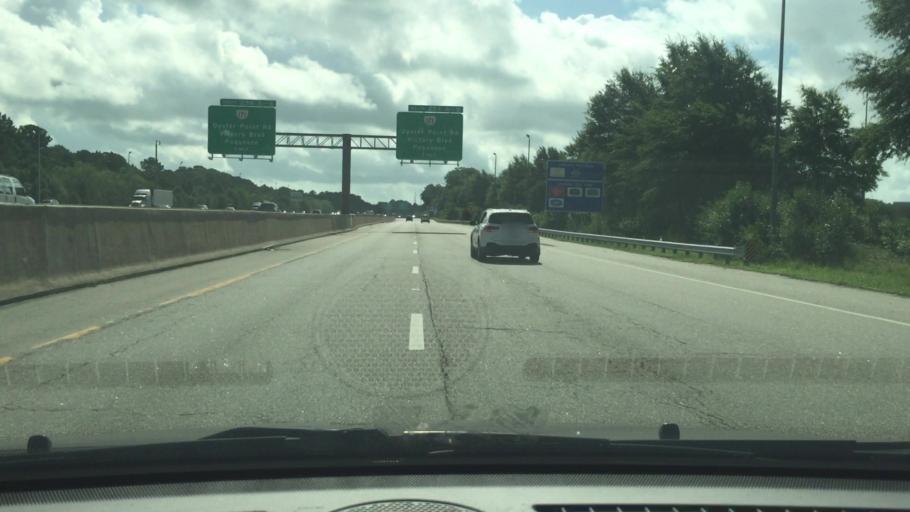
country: US
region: Virginia
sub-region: York County
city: Yorktown
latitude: 37.1151
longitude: -76.4967
